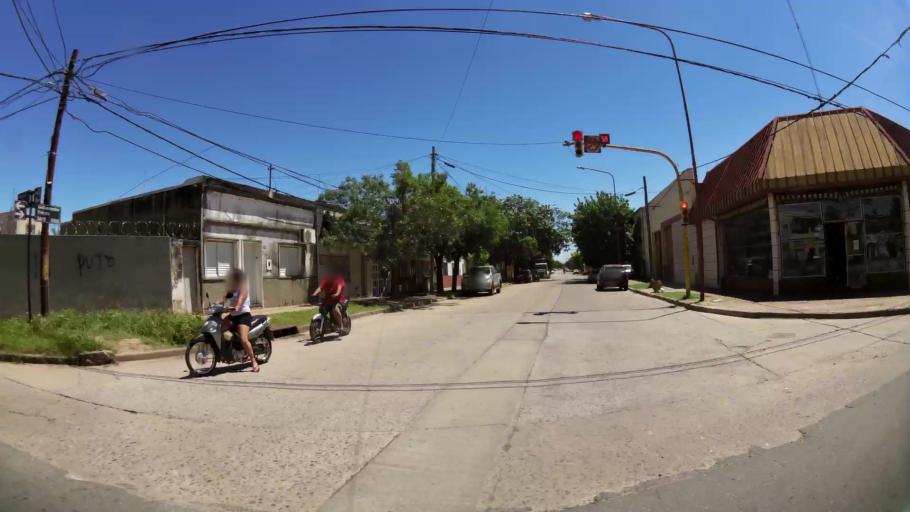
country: AR
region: Santa Fe
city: Santa Fe de la Vera Cruz
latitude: -31.6157
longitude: -60.7099
